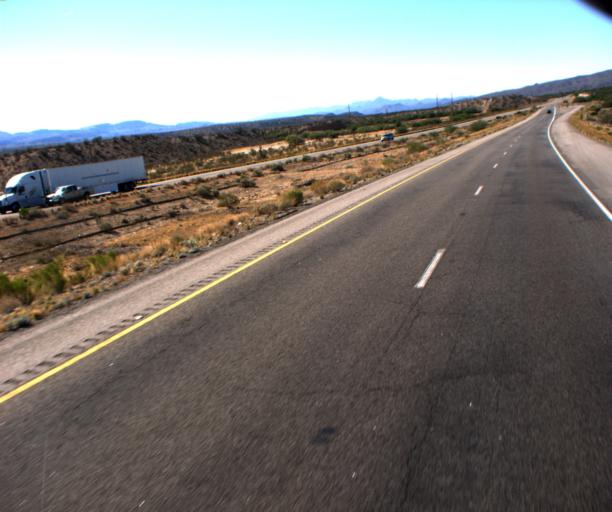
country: US
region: Arizona
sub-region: Yavapai County
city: Bagdad
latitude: 34.7453
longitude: -113.6162
